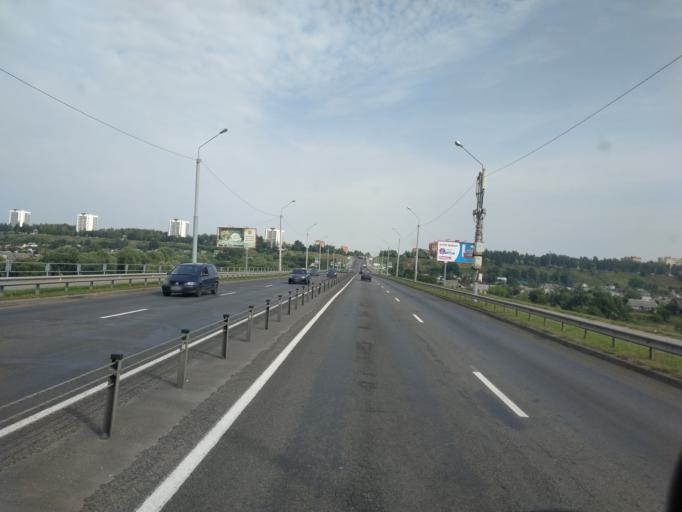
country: BY
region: Mogilev
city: Mahilyow
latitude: 53.8941
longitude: 30.3732
